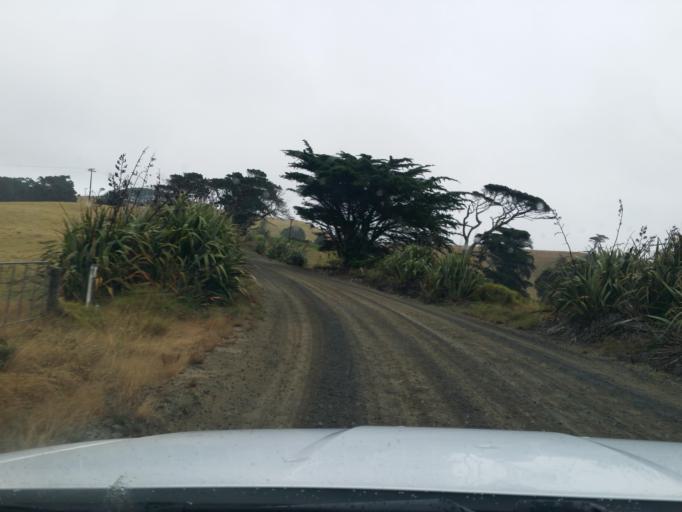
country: NZ
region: Northland
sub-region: Kaipara District
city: Dargaville
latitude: -36.0763
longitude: 173.8732
